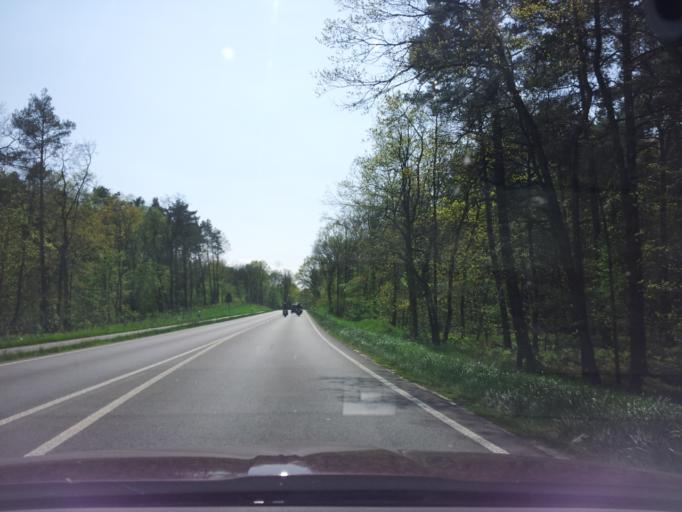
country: DE
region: Brandenburg
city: Michendorf
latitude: 52.2938
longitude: 13.0227
